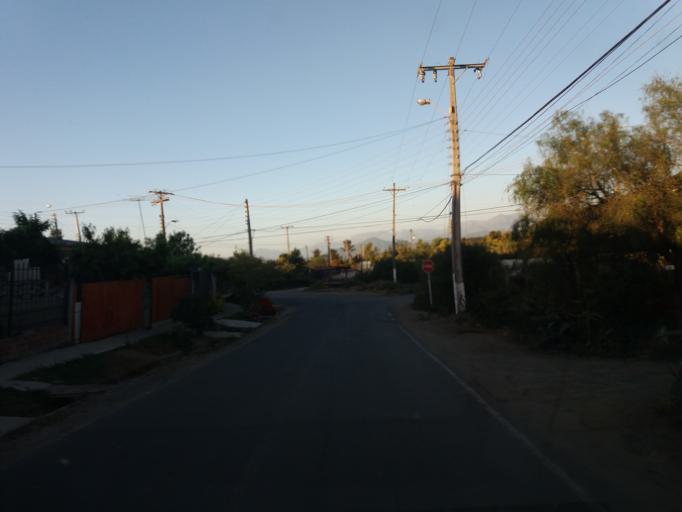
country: CL
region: Valparaiso
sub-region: Provincia de Quillota
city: Quillota
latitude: -32.9443
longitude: -71.2710
